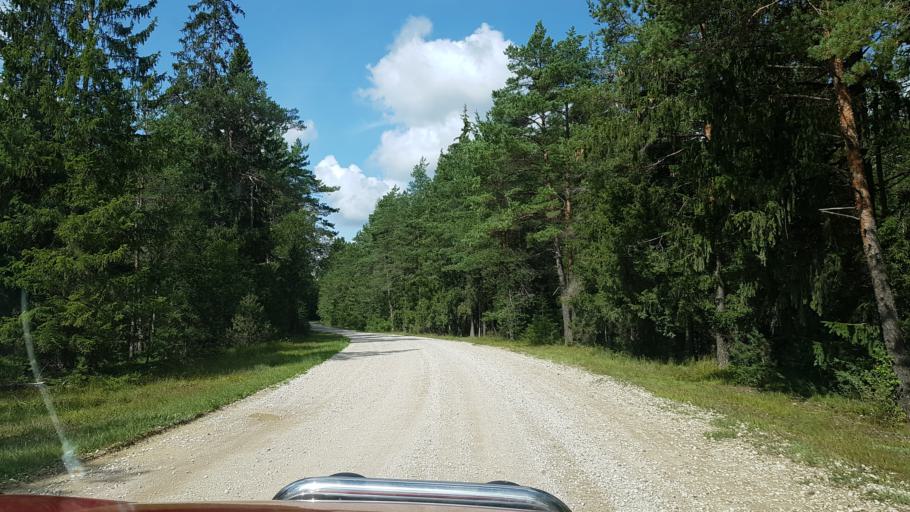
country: EE
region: Raplamaa
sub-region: Rapla vald
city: Rapla
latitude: 58.9653
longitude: 24.6361
